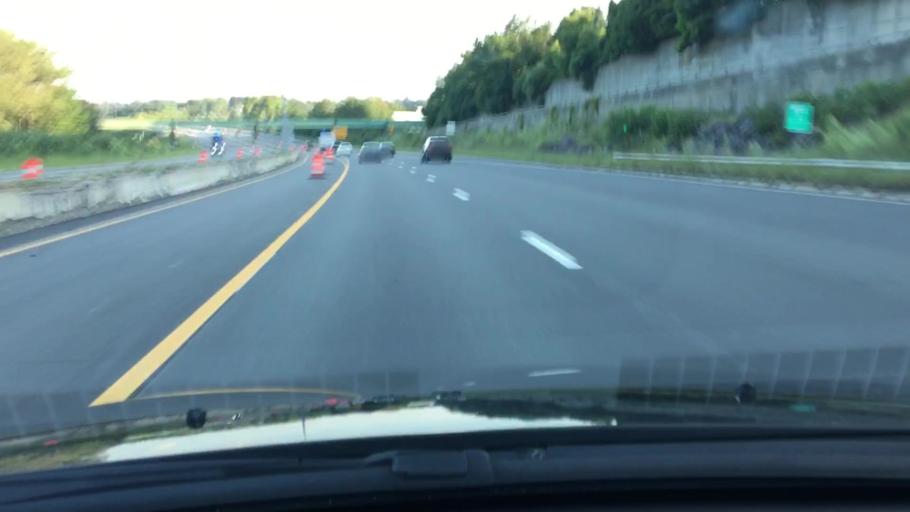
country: US
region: Massachusetts
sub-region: Worcester County
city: Worcester
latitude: 42.3080
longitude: -71.8085
